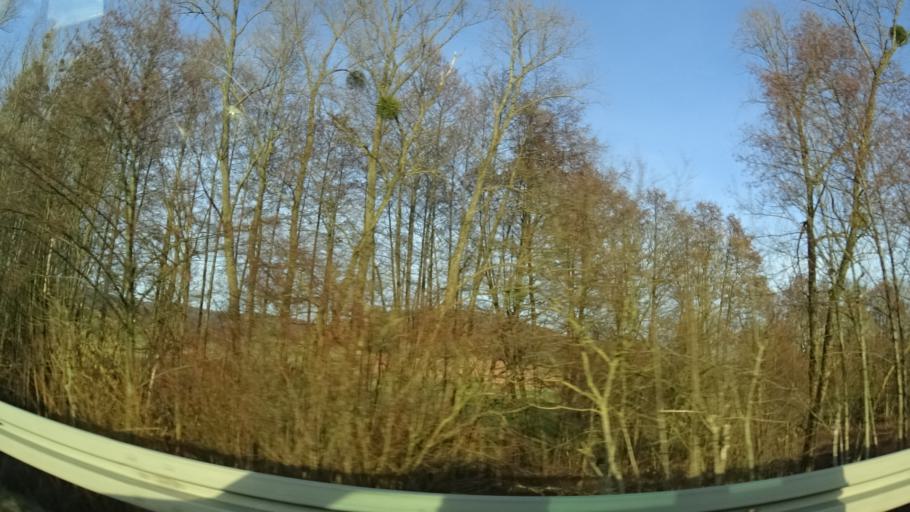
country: DE
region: Hesse
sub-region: Regierungsbezirk Darmstadt
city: Schluchtern
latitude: 50.3450
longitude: 9.5660
